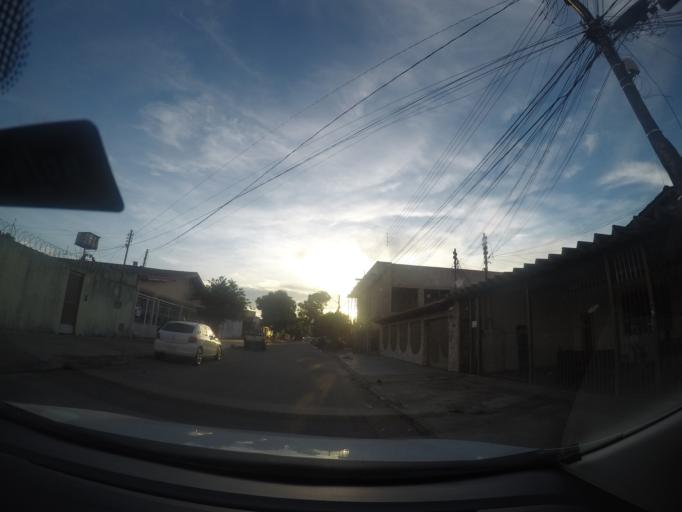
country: BR
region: Goias
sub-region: Goiania
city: Goiania
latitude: -16.6869
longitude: -49.3154
